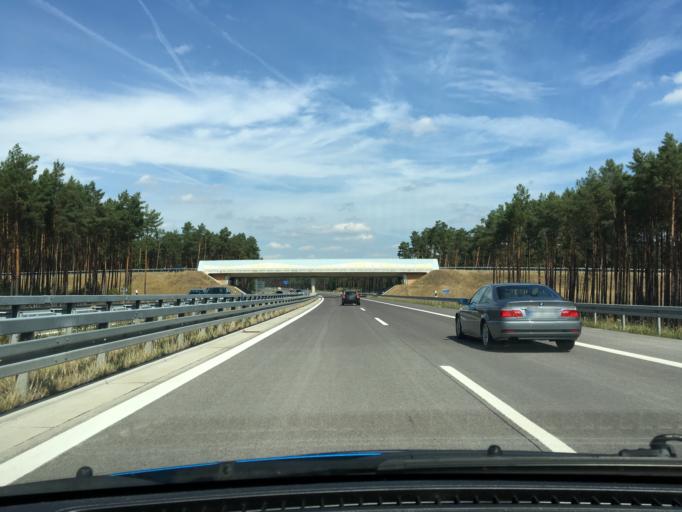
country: DE
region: Mecklenburg-Vorpommern
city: Gross Laasch
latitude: 53.3928
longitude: 11.5317
